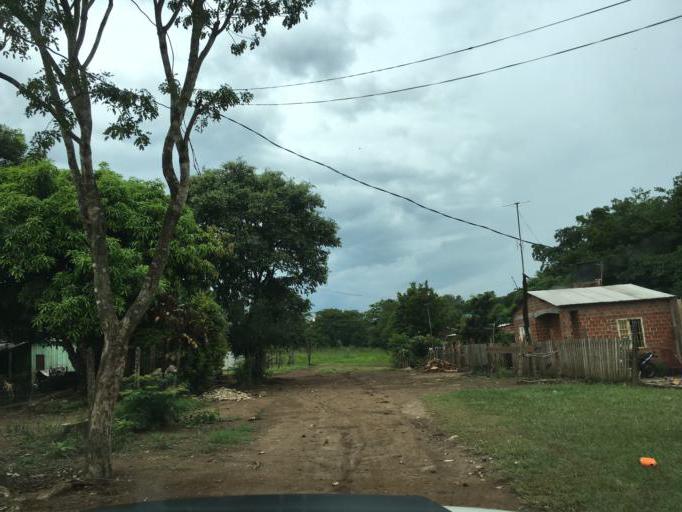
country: PY
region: Alto Parana
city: Ciudad del Este
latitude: -25.4105
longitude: -54.6507
